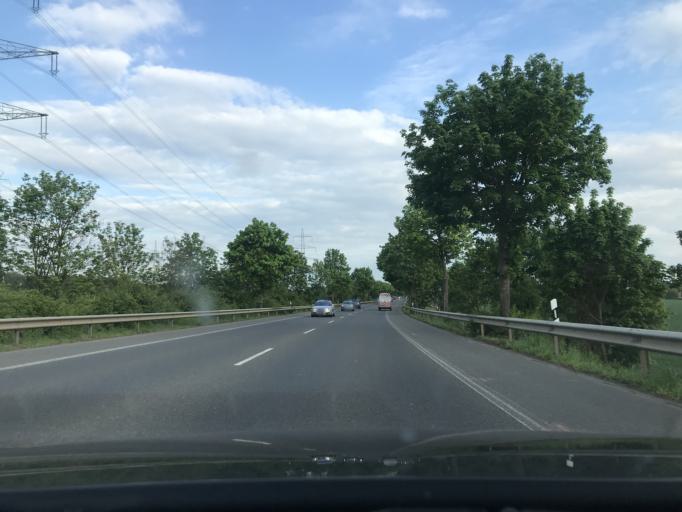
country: DE
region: North Rhine-Westphalia
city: Bornheim
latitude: 50.7766
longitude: 6.9954
